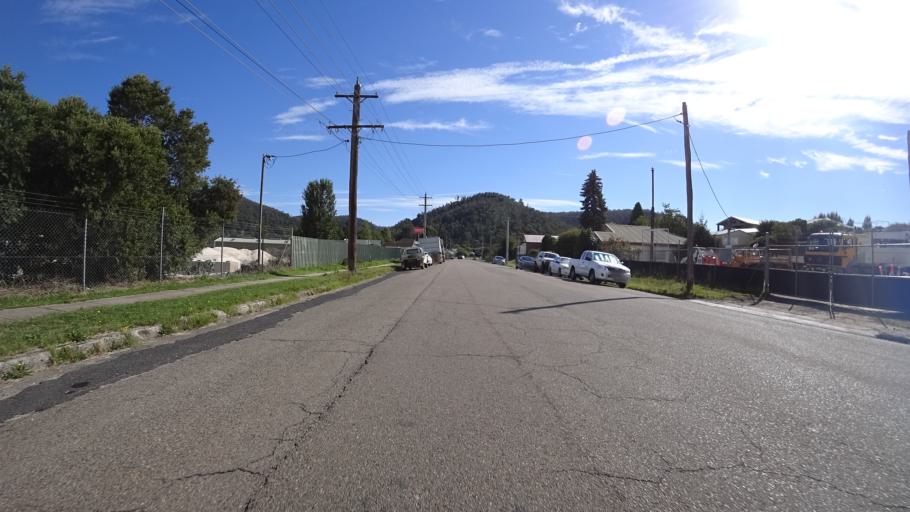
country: AU
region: New South Wales
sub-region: Lithgow
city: Lithgow
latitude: -33.4744
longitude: 150.1682
